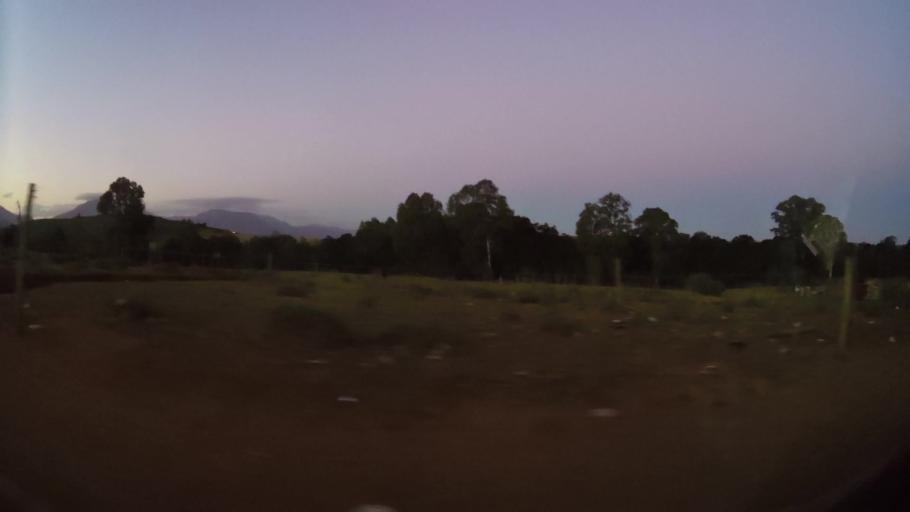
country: ZA
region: Western Cape
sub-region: Eden District Municipality
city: Riversdale
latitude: -34.1037
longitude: 21.2740
